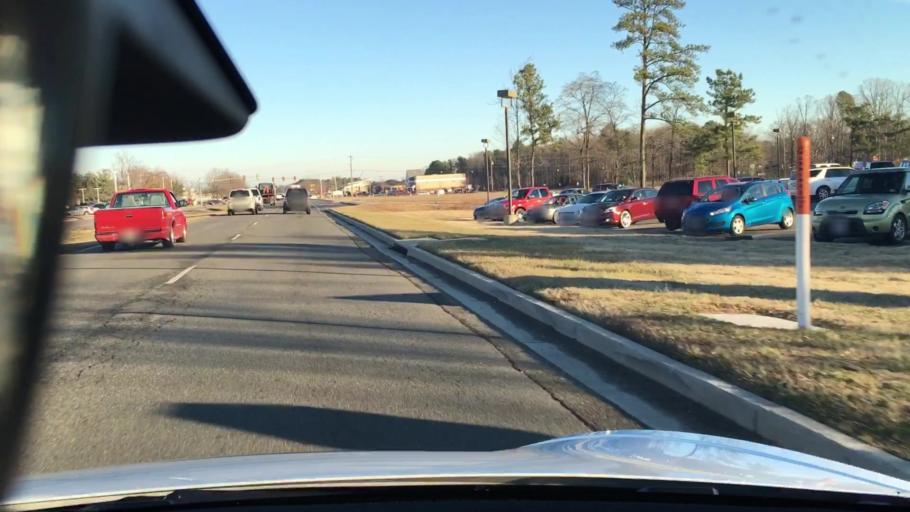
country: US
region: Virginia
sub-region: Henrico County
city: Fort Lee
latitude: 37.5090
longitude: -77.3494
